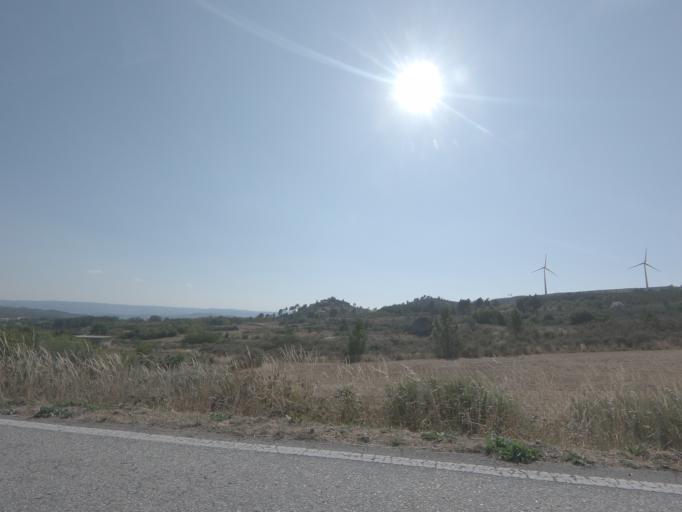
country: PT
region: Viseu
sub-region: Tabuaco
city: Tabuaco
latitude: 41.0614
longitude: -7.5620
